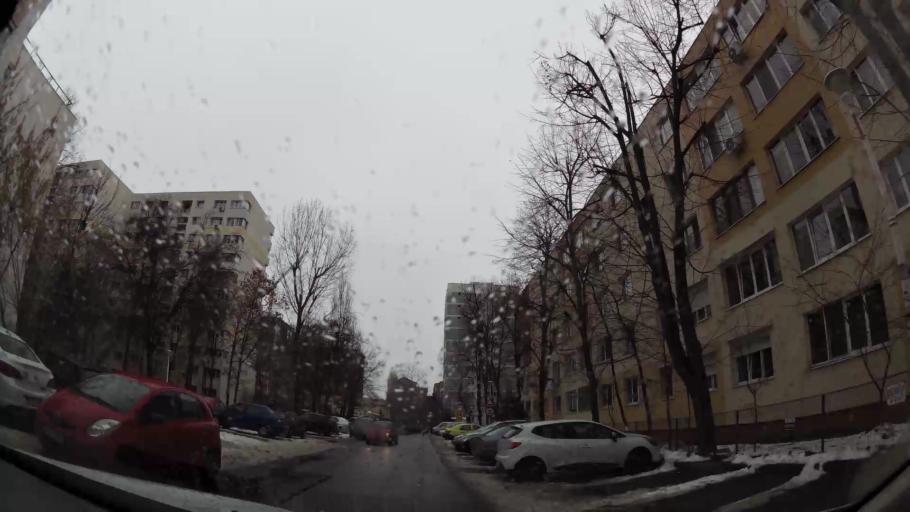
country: RO
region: Ilfov
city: Dobroesti
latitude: 44.4222
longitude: 26.1694
